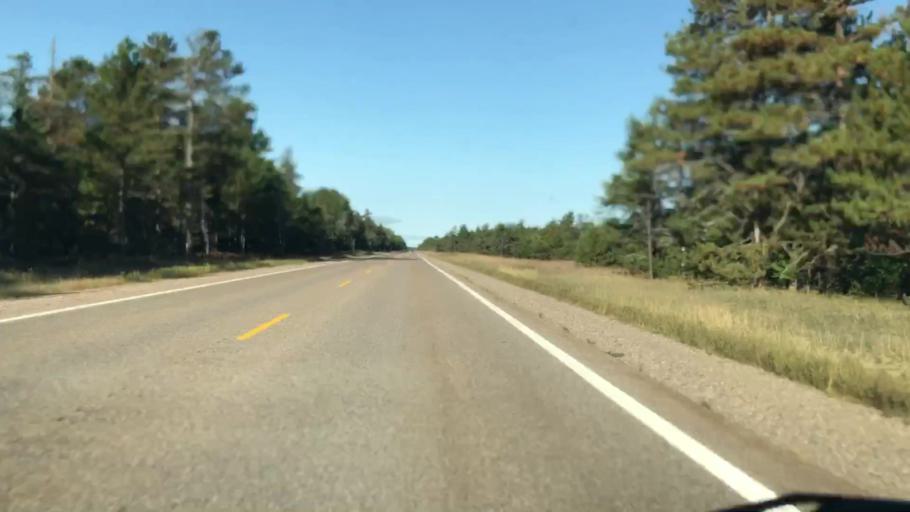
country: US
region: Michigan
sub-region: Mackinac County
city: Saint Ignace
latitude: 46.3586
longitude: -84.8414
